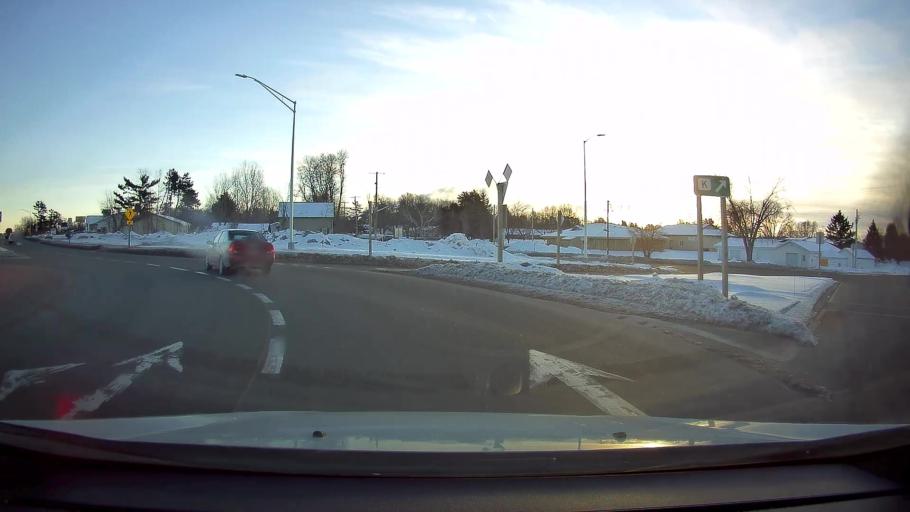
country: US
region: Wisconsin
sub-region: Barron County
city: Turtle Lake
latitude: 45.3958
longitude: -92.1517
